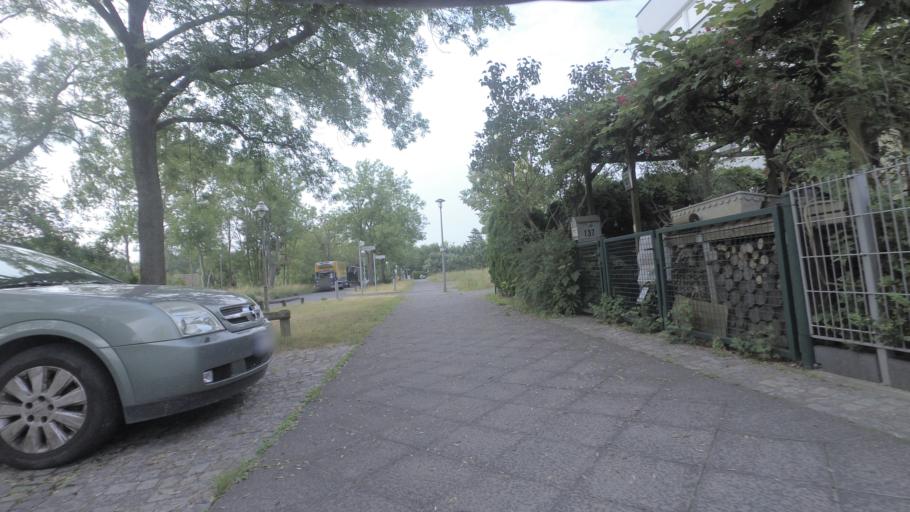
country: DE
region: Brandenburg
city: Schonefeld
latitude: 52.4027
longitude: 13.5006
